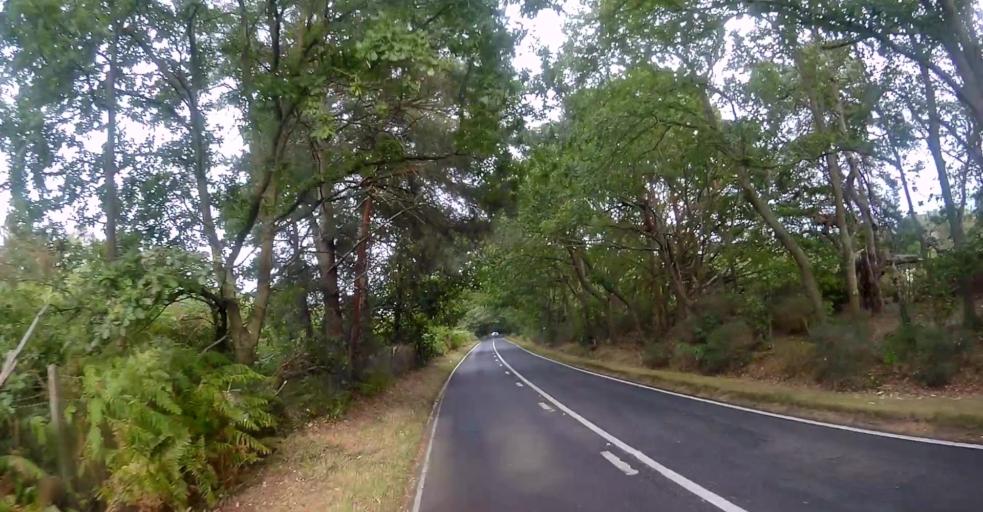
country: GB
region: England
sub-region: Surrey
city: Pirbright
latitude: 51.2998
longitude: -0.6742
